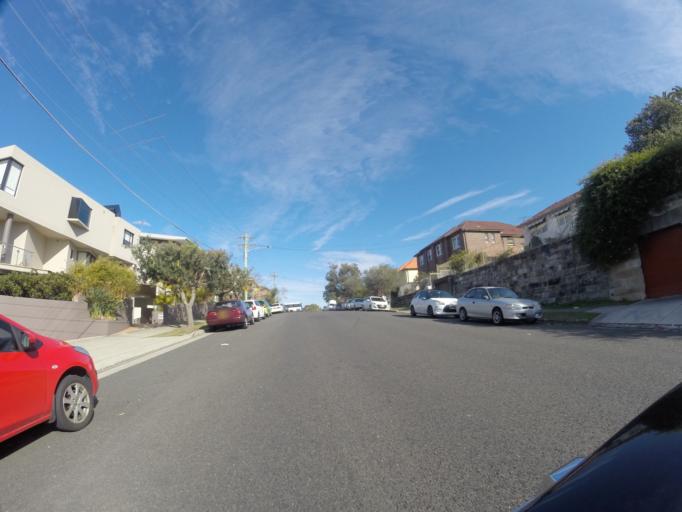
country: AU
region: New South Wales
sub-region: Randwick
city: Coogee
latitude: -33.9255
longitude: 151.2534
